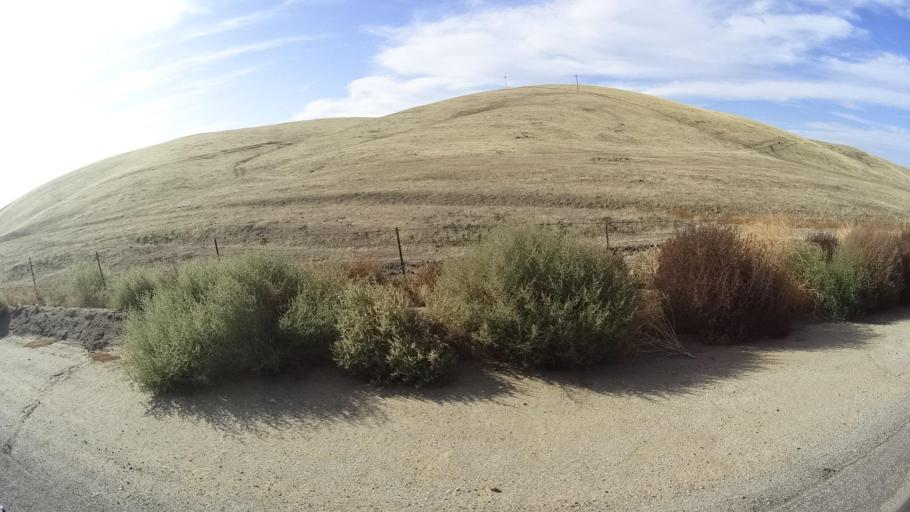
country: US
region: California
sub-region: Kern County
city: Oildale
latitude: 35.6064
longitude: -118.9564
